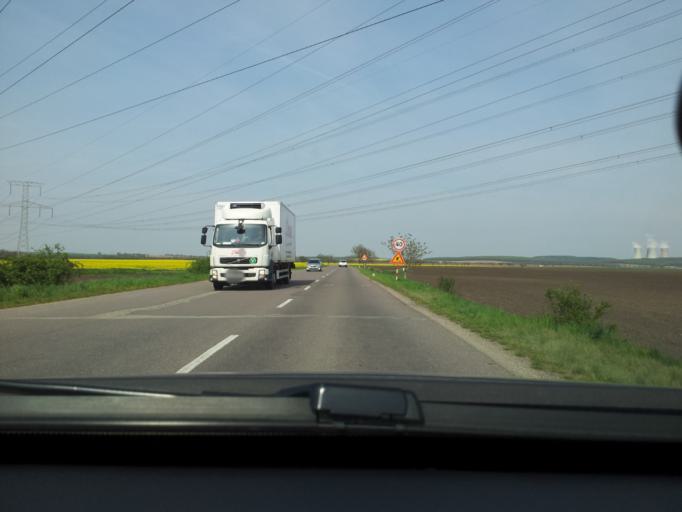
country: SK
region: Nitriansky
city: Tlmace
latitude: 48.2149
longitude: 18.5139
